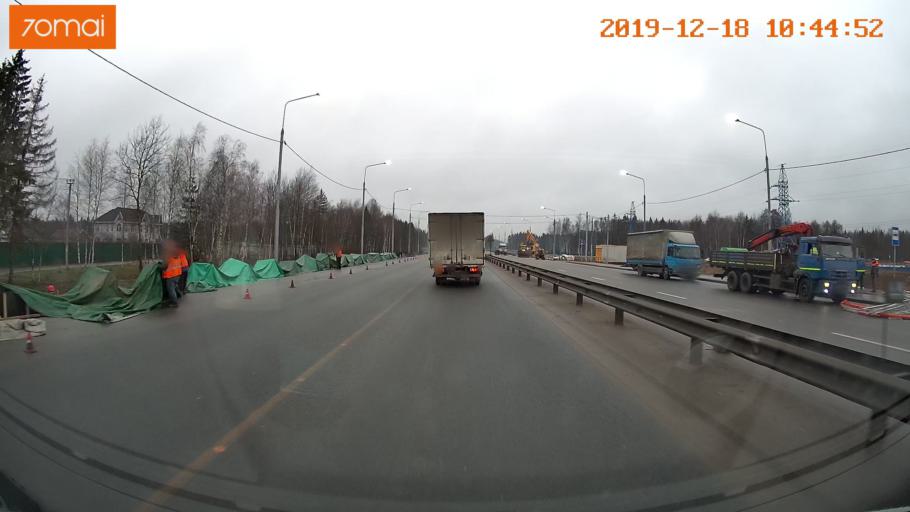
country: RU
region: Moskovskaya
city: Aprelevka
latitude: 55.4750
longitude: 37.0673
